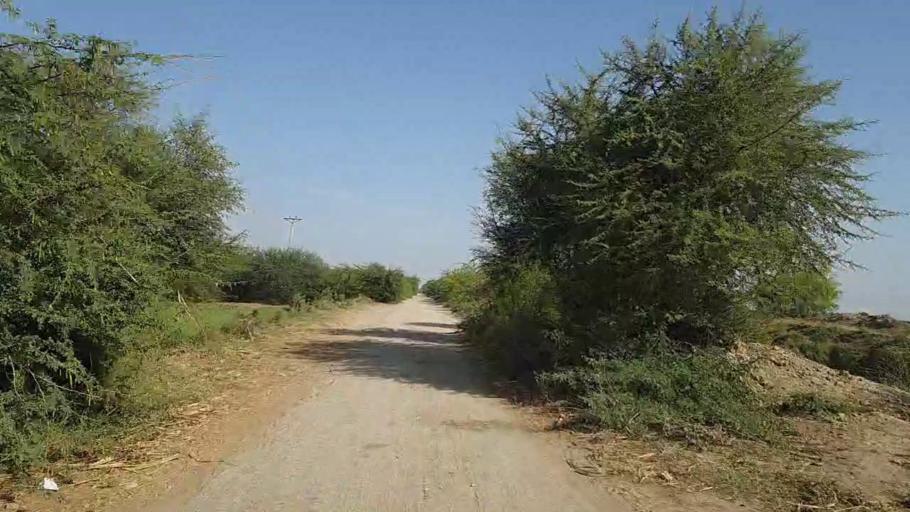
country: PK
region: Sindh
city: Kotri
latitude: 25.1668
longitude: 68.2885
